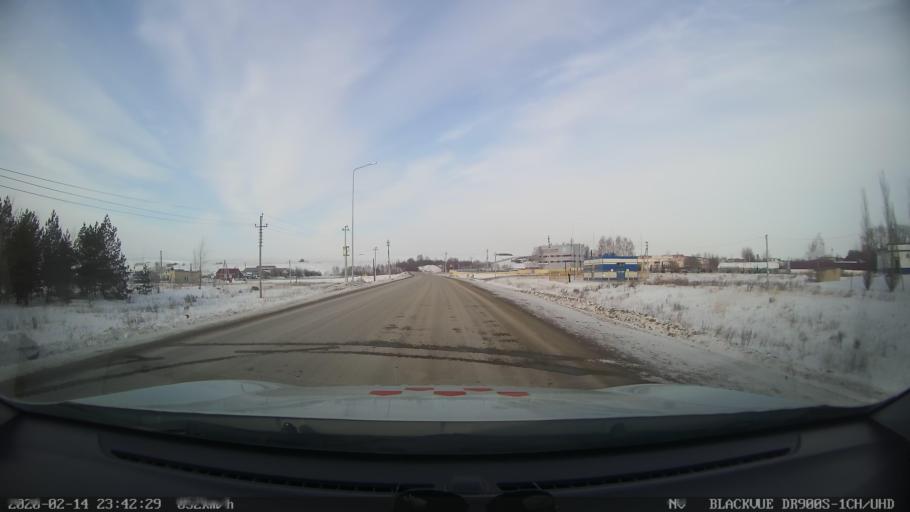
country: RU
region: Tatarstan
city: Kuybyshevskiy Zaton
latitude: 55.1920
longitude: 49.2471
